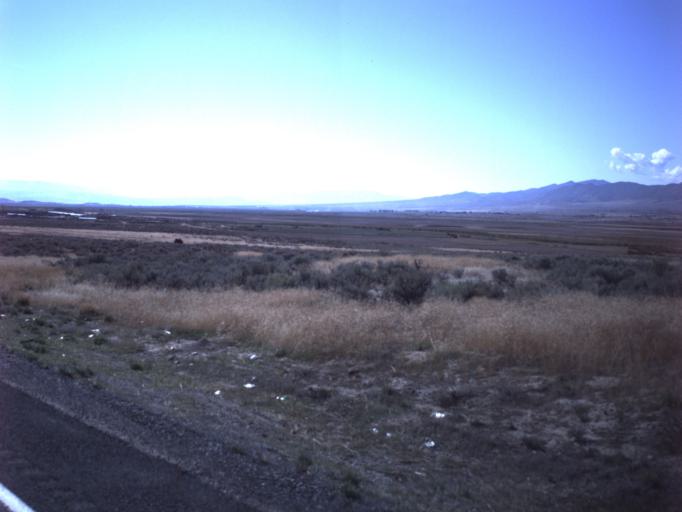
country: US
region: Utah
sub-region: Sanpete County
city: Gunnison
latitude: 39.2759
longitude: -111.8760
